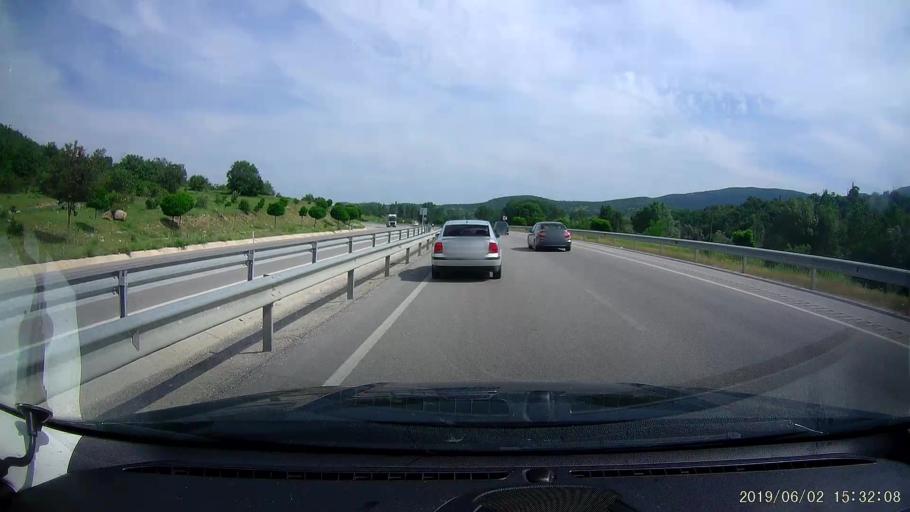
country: TR
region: Amasya
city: Saraycik
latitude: 40.9400
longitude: 35.1361
